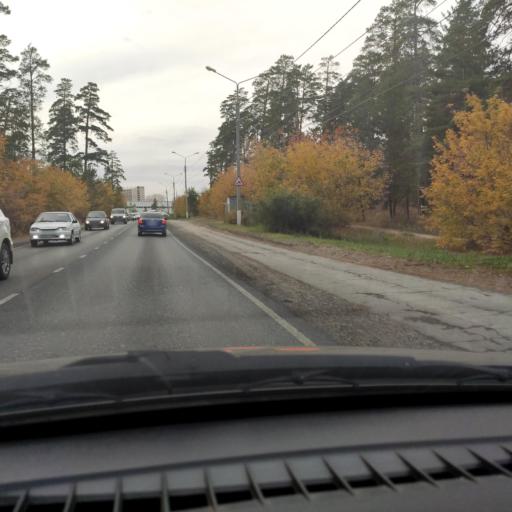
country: RU
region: Samara
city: Tol'yatti
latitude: 53.4762
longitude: 49.3296
